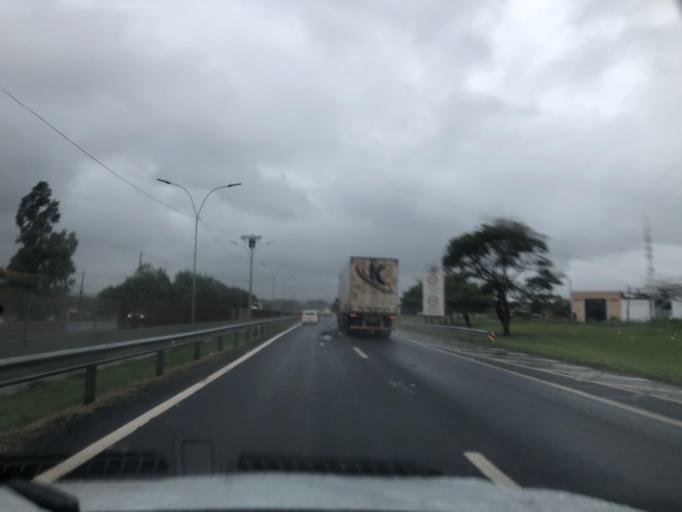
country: BR
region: Sao Paulo
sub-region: Ribeirao Preto
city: Ribeirao Preto
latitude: -21.1248
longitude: -47.7718
